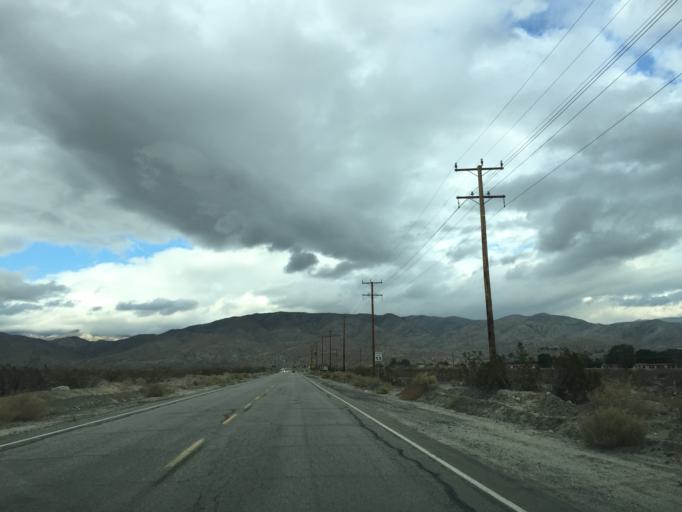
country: US
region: California
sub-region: Riverside County
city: Desert Hot Springs
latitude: 33.9728
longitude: -116.5449
